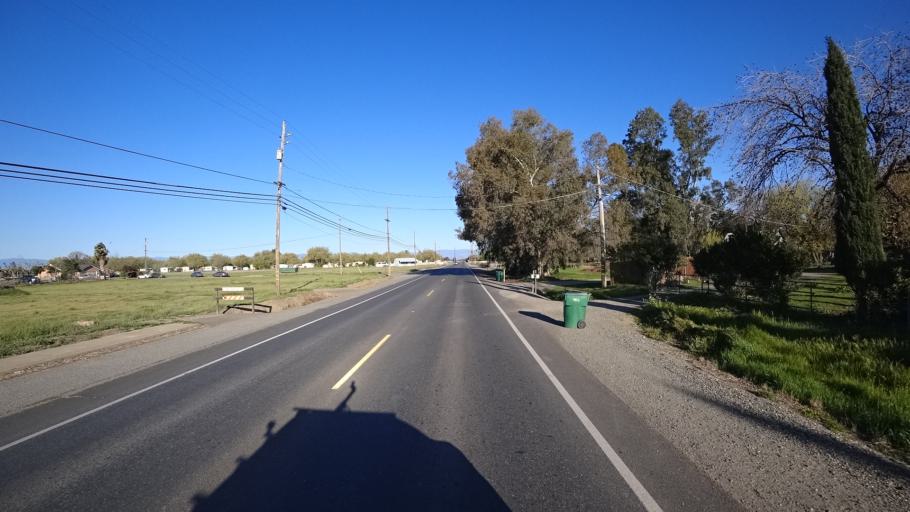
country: US
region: California
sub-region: Glenn County
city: Orland
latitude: 39.7530
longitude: -122.2114
